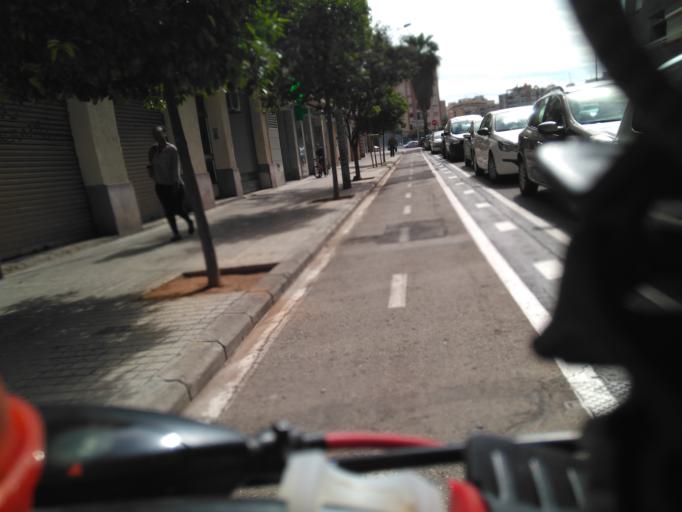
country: ES
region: Valencia
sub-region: Provincia de Valencia
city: Valencia
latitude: 39.4863
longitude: -0.3900
